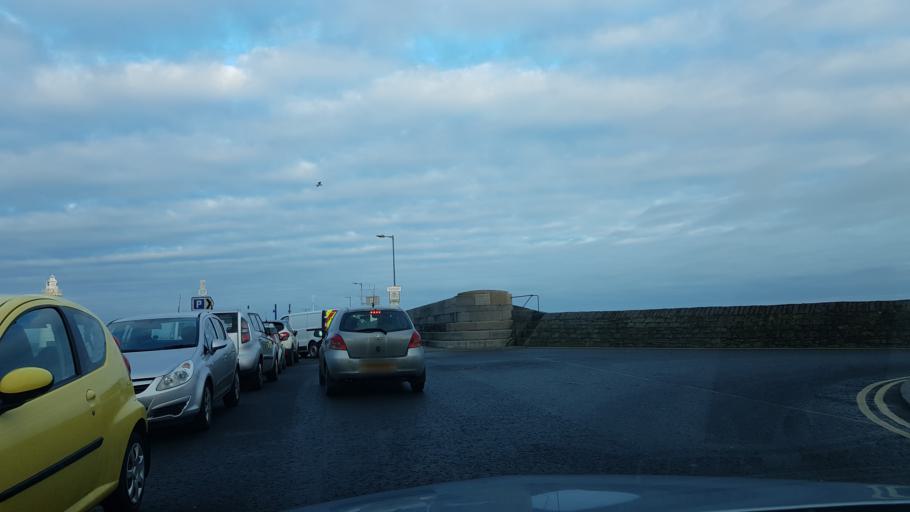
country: GB
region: Northern Ireland
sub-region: Down District
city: Donaghadee
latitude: 54.6435
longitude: -5.5321
